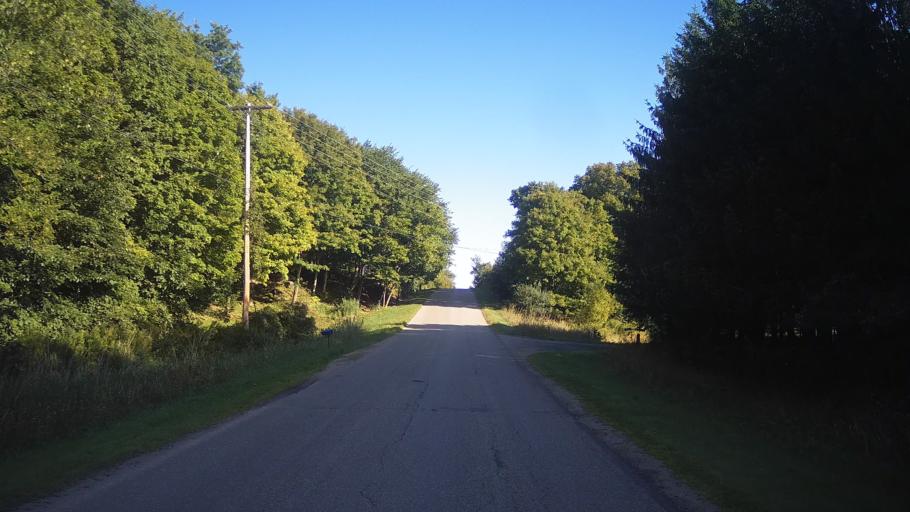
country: US
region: New York
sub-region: Jefferson County
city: Alexandria Bay
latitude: 44.4476
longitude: -75.9846
